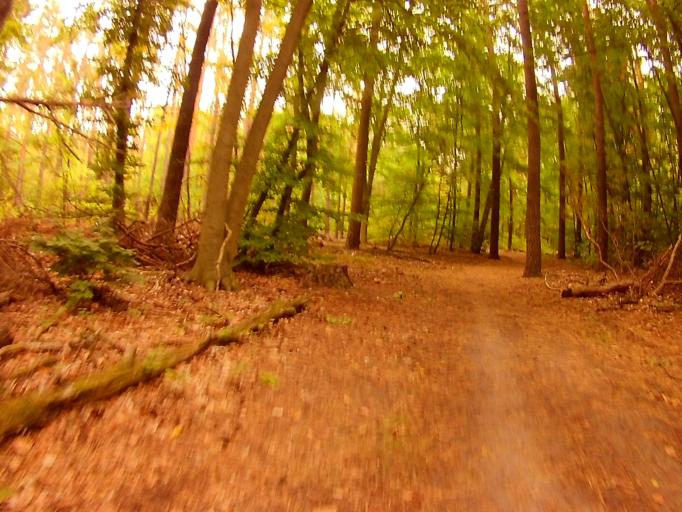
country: DE
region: Berlin
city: Grunau
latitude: 52.4068
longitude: 13.5959
